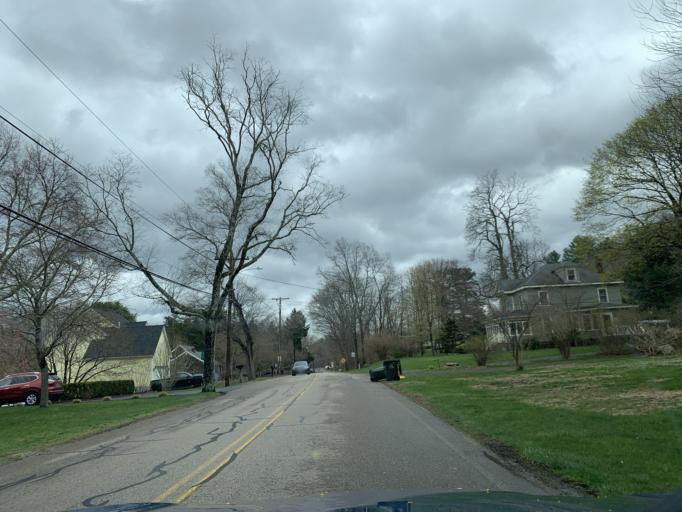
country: US
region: Massachusetts
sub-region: Bristol County
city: Norton
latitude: 41.9529
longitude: -71.2313
